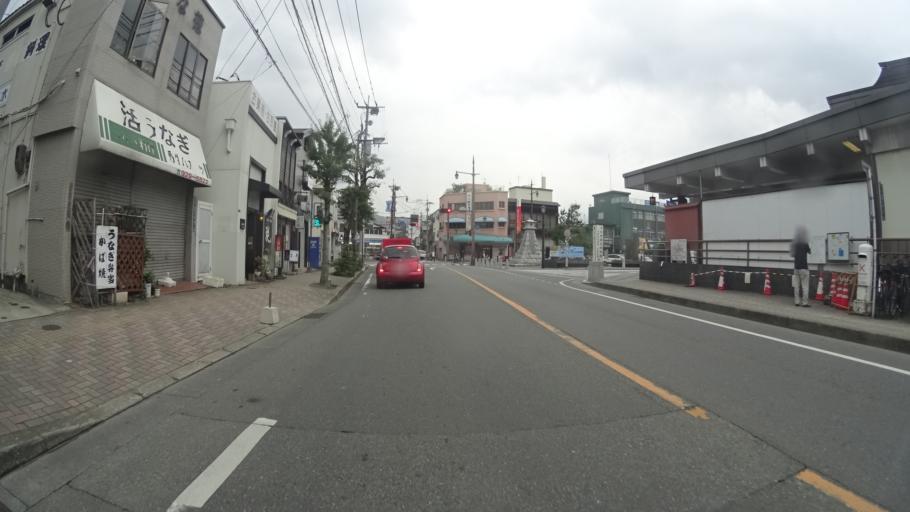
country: JP
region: Fukuoka
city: Dazaifu
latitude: 33.5191
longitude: 130.5311
